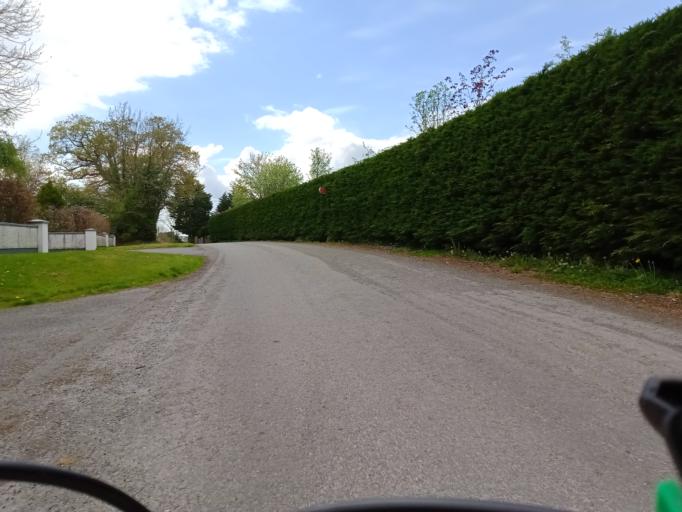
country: IE
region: Leinster
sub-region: Kilkenny
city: Kilkenny
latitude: 52.6312
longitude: -7.2852
